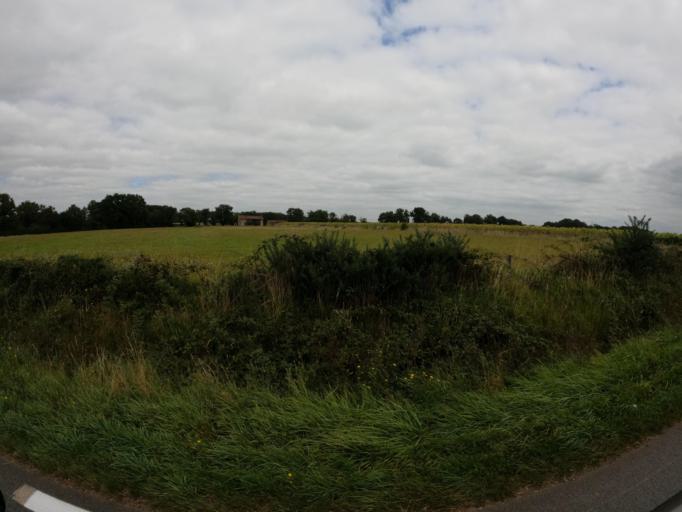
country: FR
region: Poitou-Charentes
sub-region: Departement de la Vienne
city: Availles-Limouzine
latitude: 46.1196
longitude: 0.5318
